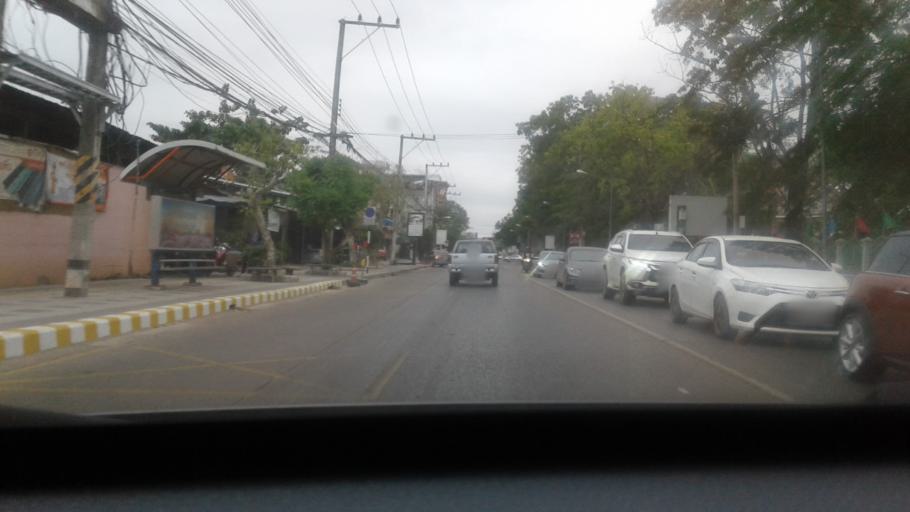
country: TH
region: Changwat Udon Thani
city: Udon Thani
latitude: 17.4029
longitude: 102.7907
